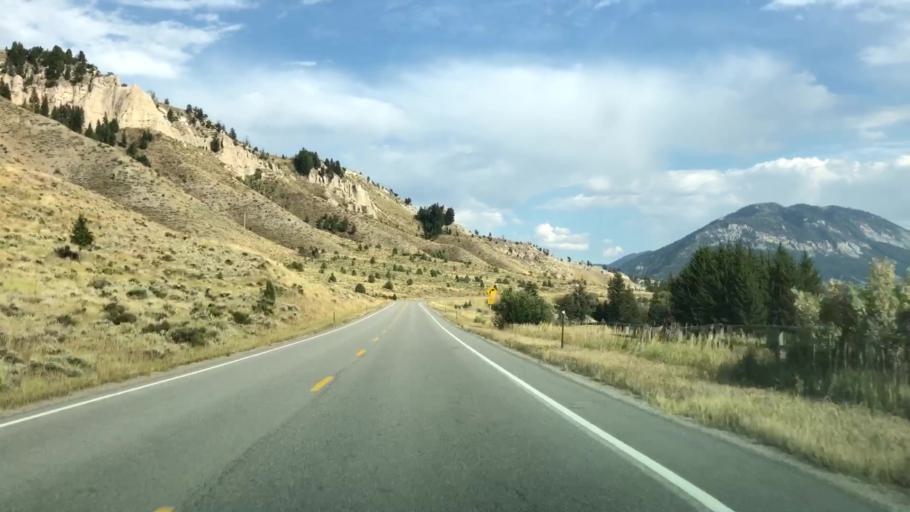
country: US
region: Wyoming
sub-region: Teton County
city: Hoback
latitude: 43.3143
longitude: -110.6881
